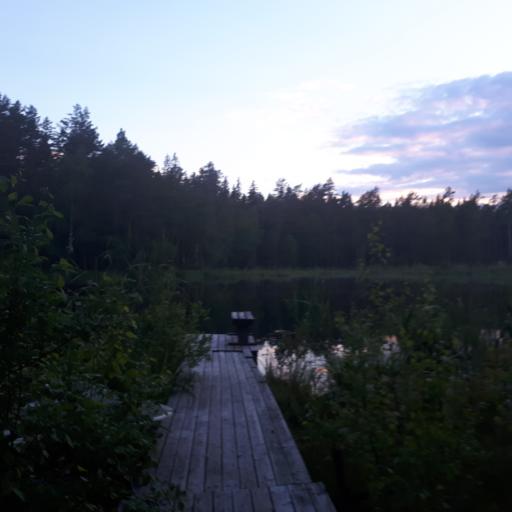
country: SE
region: Soedermanland
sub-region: Flens Kommun
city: Halleforsnas
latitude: 59.0860
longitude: 16.3932
